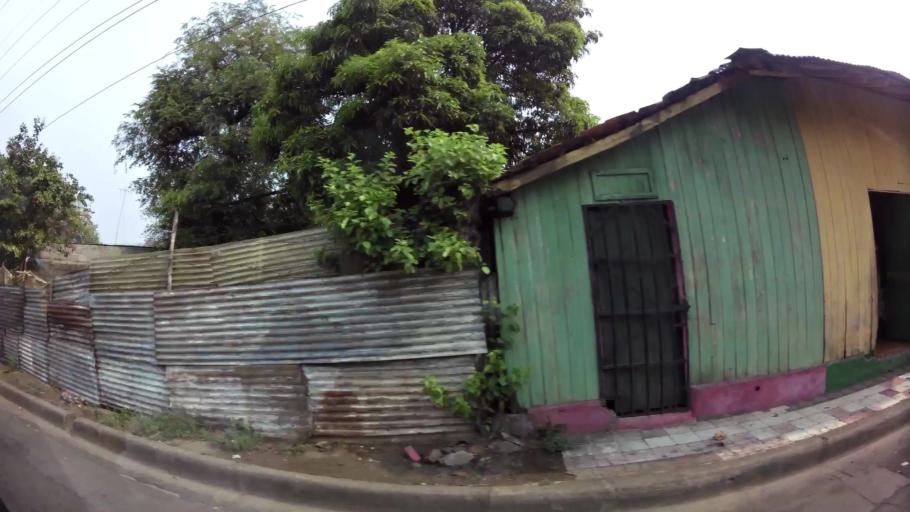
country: NI
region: Chinandega
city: Chinandega
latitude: 12.6239
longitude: -87.1334
